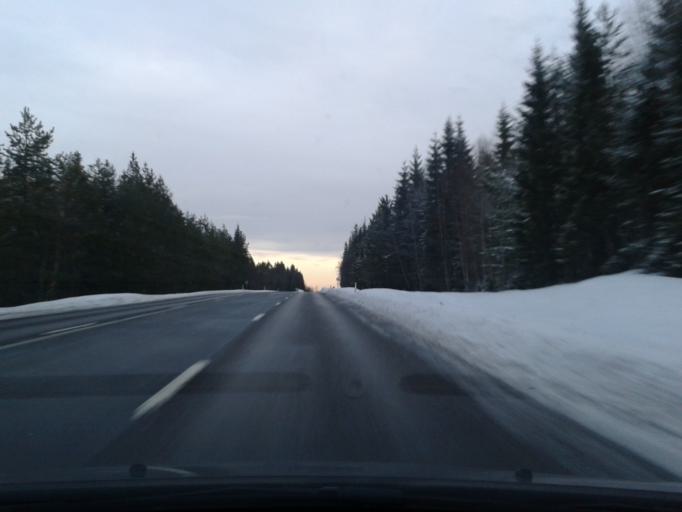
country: SE
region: Vaesternorrland
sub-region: Solleftea Kommun
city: Solleftea
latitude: 63.1245
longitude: 17.4854
